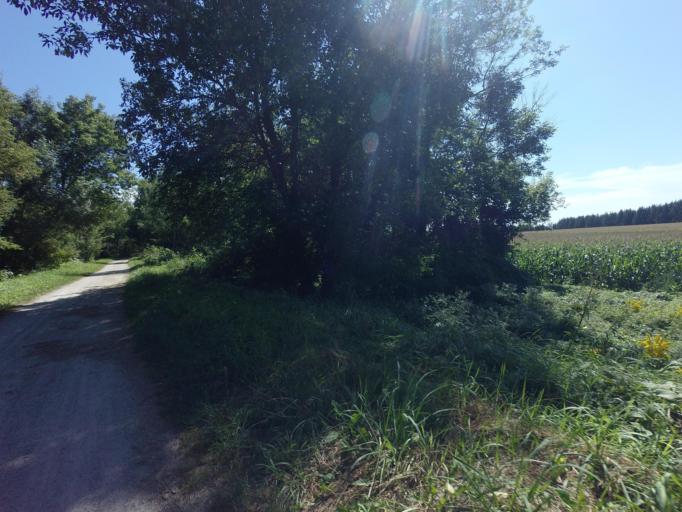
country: CA
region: Ontario
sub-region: Wellington County
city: Guelph
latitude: 43.7399
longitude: -80.3596
